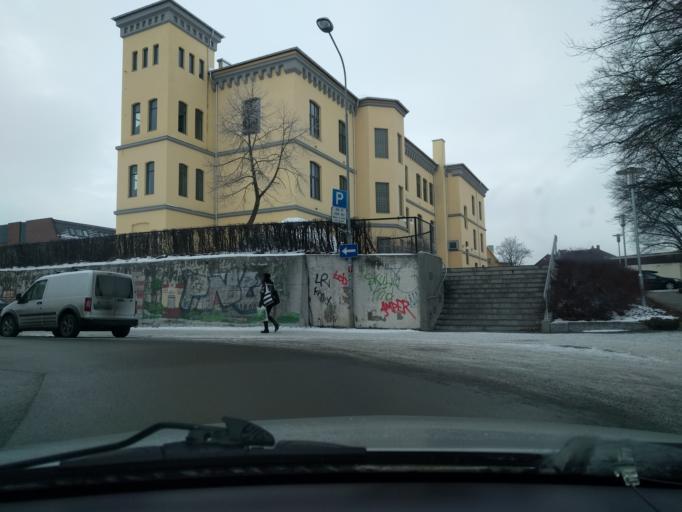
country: NO
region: Hedmark
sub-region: Hamar
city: Hamar
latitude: 60.7956
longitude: 11.0740
